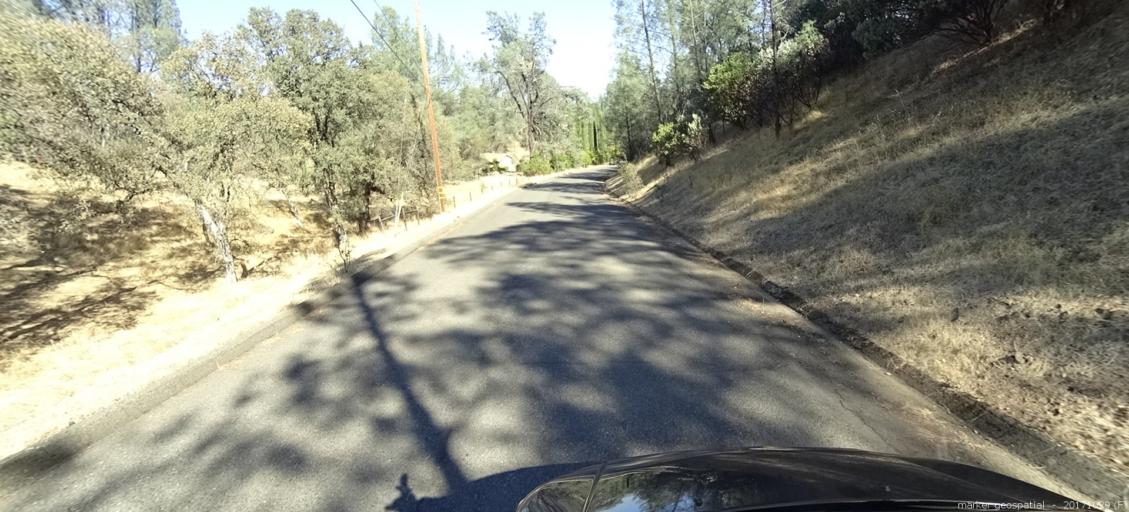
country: US
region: California
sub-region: Shasta County
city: Anderson
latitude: 40.4790
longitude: -122.3546
